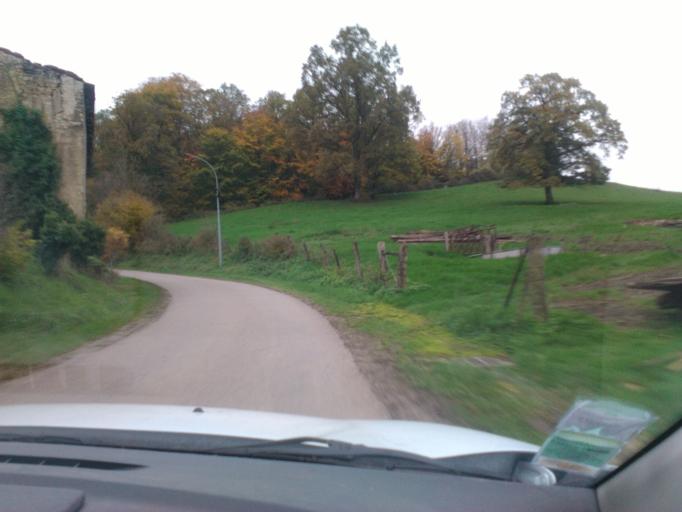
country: FR
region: Lorraine
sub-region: Departement des Vosges
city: Mirecourt
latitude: 48.3109
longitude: 6.2092
